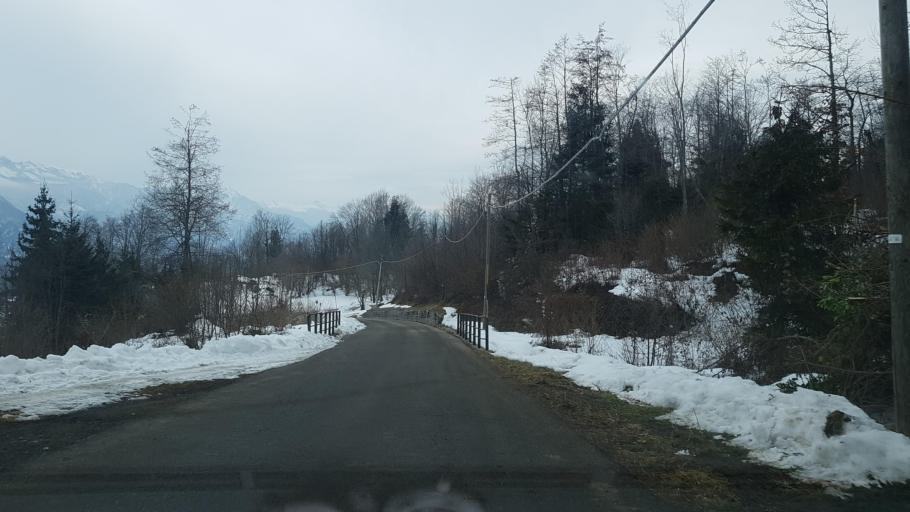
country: IT
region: Friuli Venezia Giulia
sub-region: Provincia di Udine
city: Lauco
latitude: 46.4284
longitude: 12.9357
